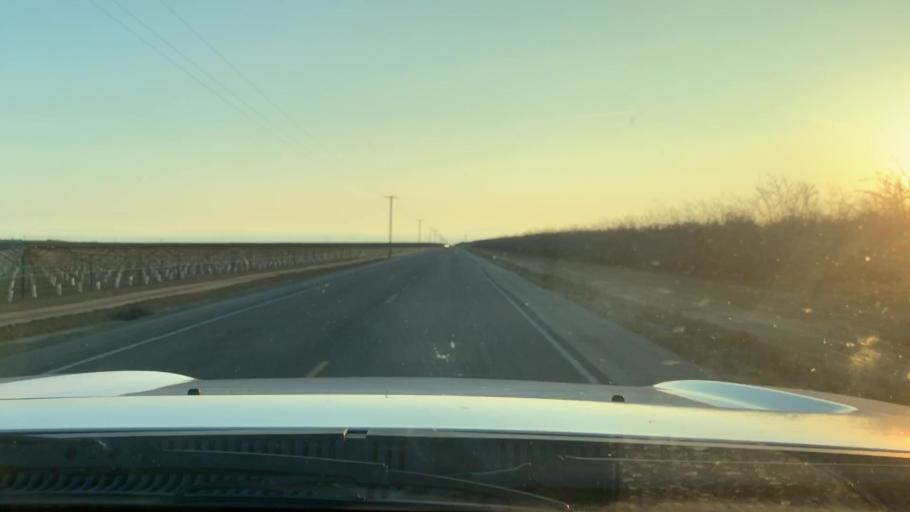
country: US
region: California
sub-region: Kern County
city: Buttonwillow
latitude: 35.5005
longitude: -119.4293
